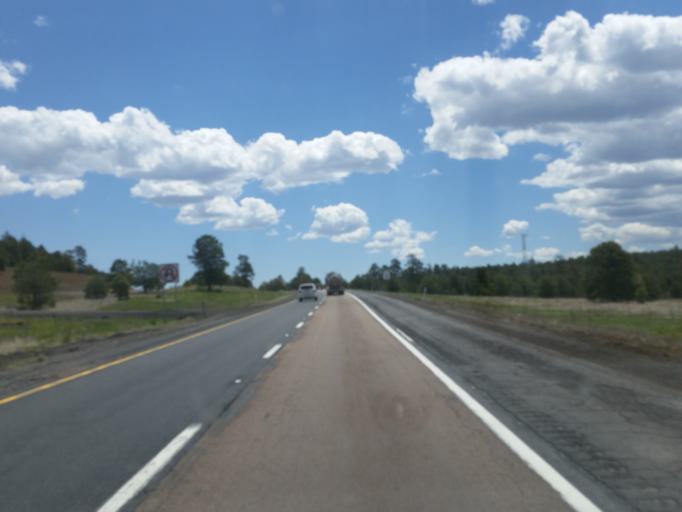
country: US
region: Arizona
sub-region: Coconino County
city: Flagstaff
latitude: 35.2000
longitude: -111.7560
